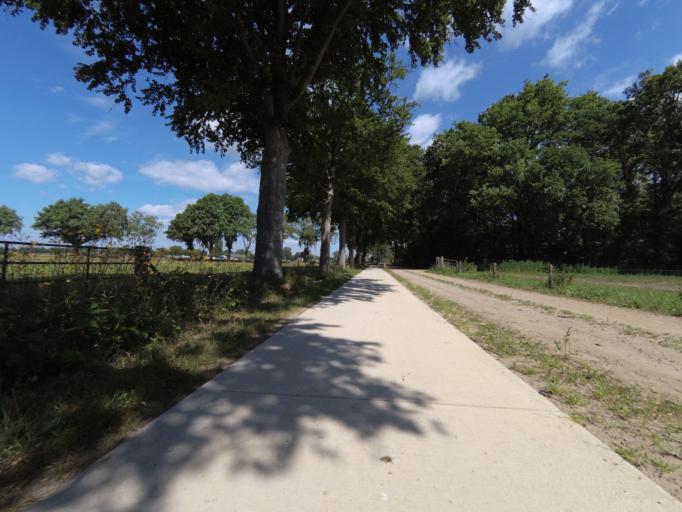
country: NL
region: Gelderland
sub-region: Gemeente Voorst
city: Twello
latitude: 52.1868
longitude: 6.0873
